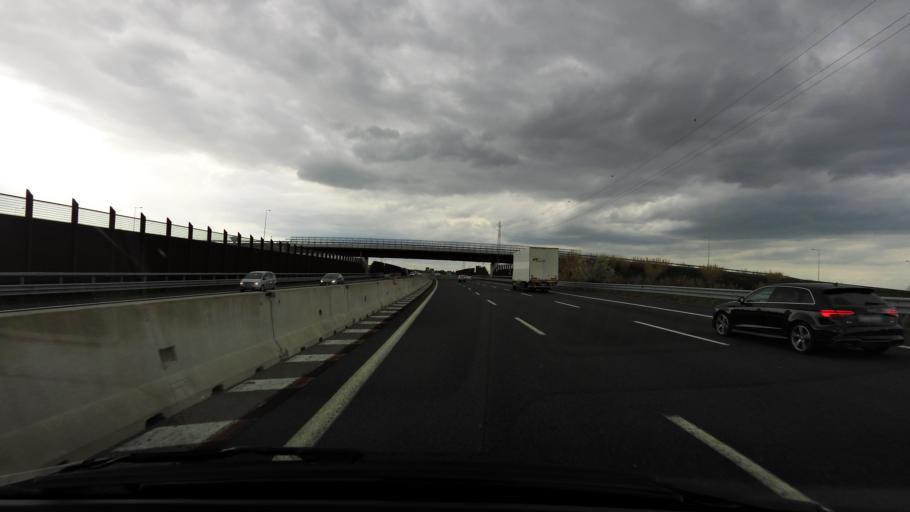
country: IT
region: Emilia-Romagna
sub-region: Provincia di Rimini
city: Santa Giustina
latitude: 44.0778
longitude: 12.4848
